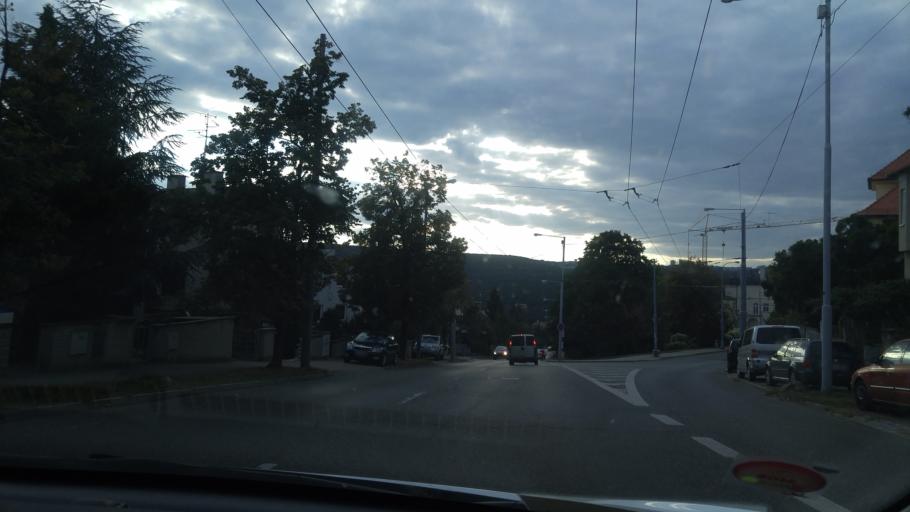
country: CZ
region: South Moravian
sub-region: Mesto Brno
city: Brno
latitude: 49.1946
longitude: 16.5840
